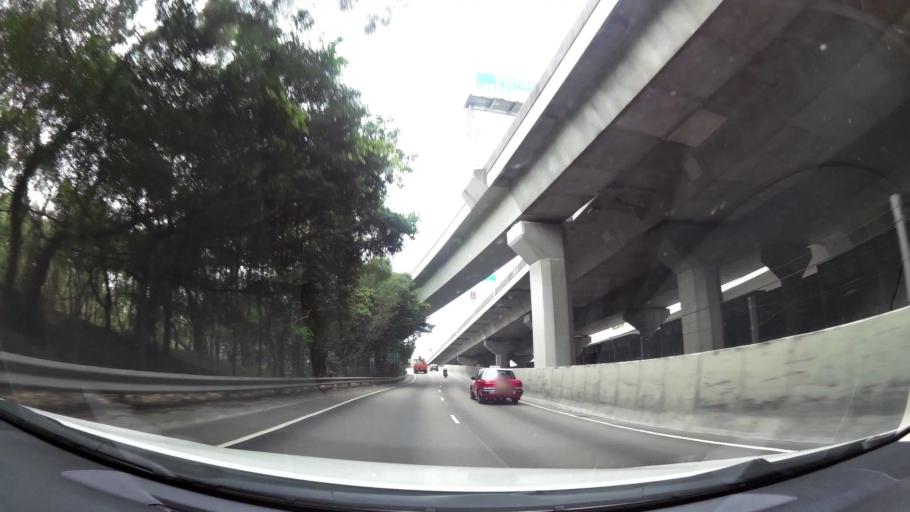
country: HK
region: Sham Shui Po
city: Sham Shui Po
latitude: 22.3314
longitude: 114.1426
